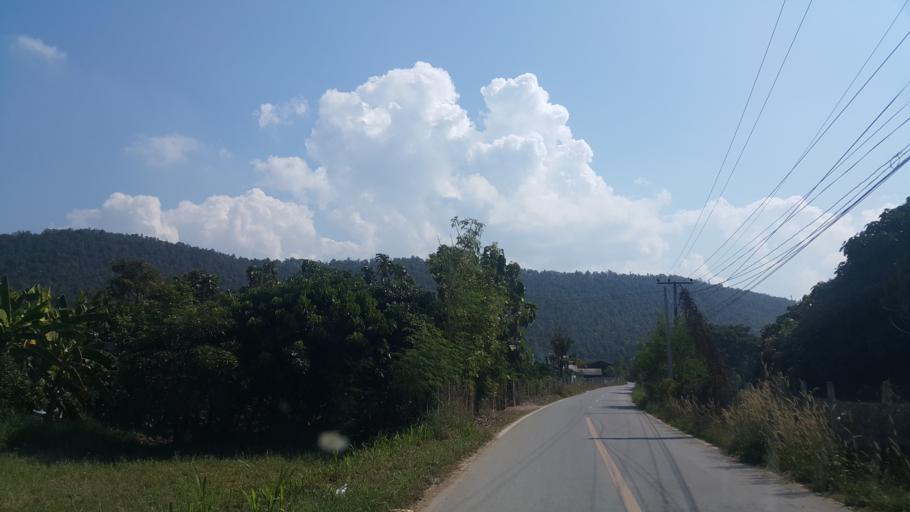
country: TH
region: Chiang Mai
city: San Kamphaeng
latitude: 18.6964
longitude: 99.1654
